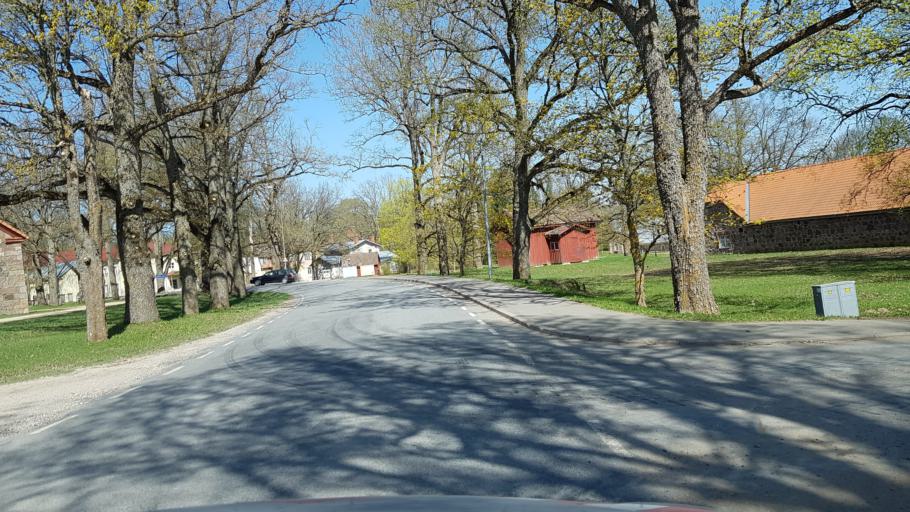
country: EE
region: Viljandimaa
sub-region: Vohma linn
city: Vohma
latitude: 58.5520
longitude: 25.5651
